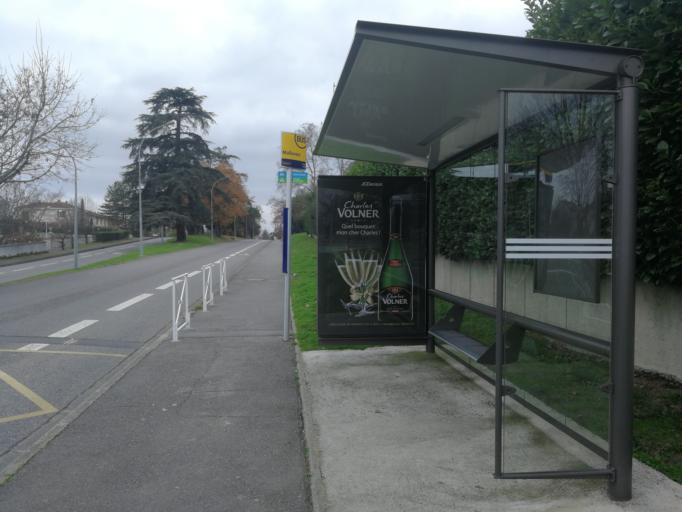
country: FR
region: Midi-Pyrenees
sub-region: Departement de la Haute-Garonne
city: Balma
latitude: 43.6038
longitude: 1.5043
